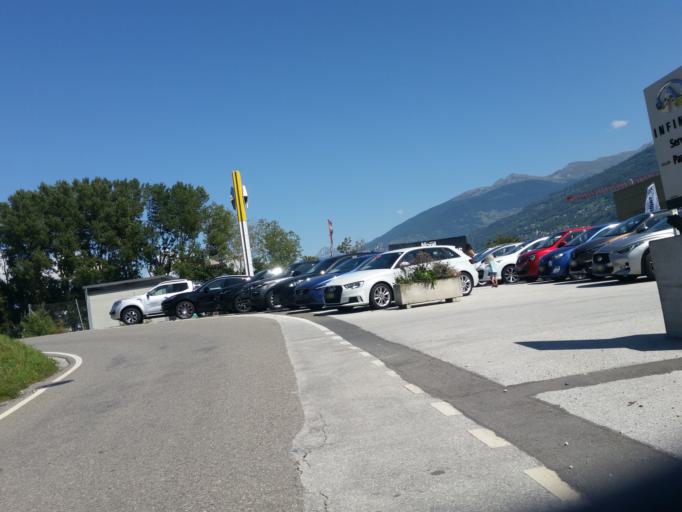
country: CH
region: Valais
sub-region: Conthey District
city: Vetroz
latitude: 46.2150
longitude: 7.2924
